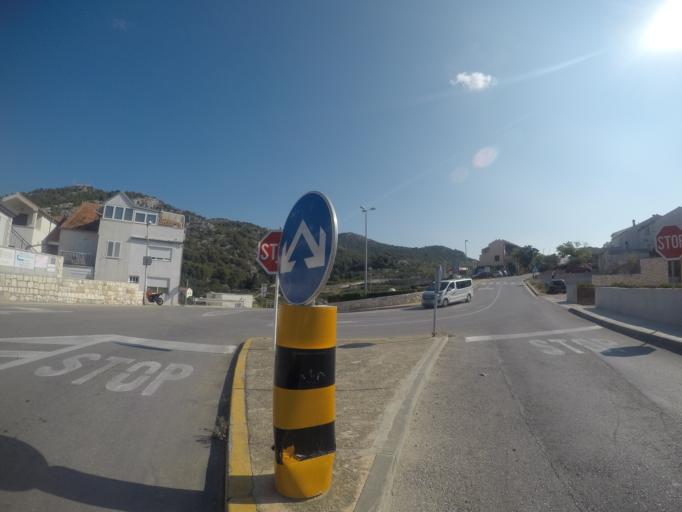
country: HR
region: Splitsko-Dalmatinska
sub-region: Grad Hvar
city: Hvar
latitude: 43.1705
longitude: 16.4465
